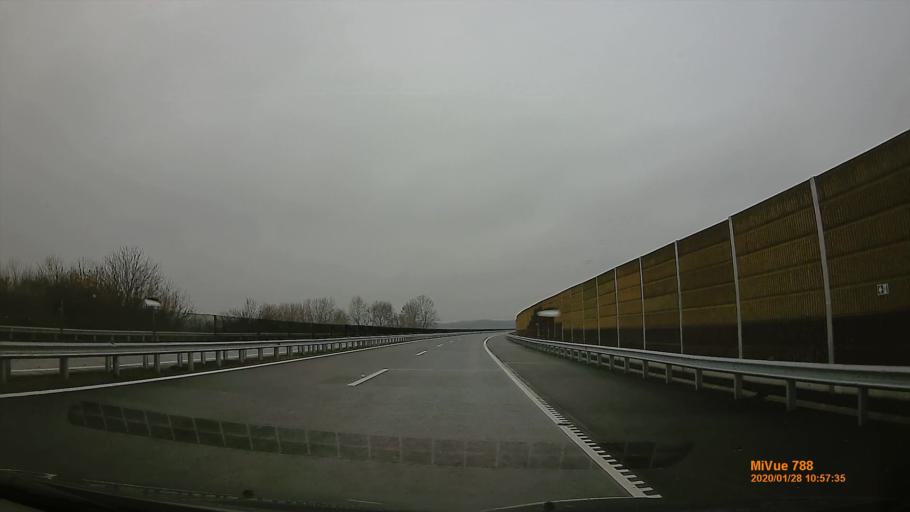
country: HU
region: Pest
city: Peteri
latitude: 47.3728
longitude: 19.4136
